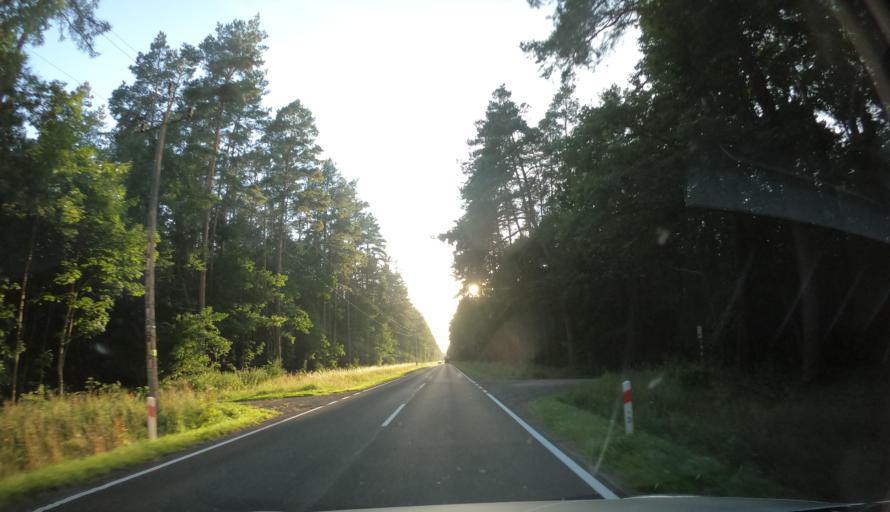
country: PL
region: Kujawsko-Pomorskie
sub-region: Powiat bydgoski
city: Koronowo
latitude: 53.3093
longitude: 18.0437
